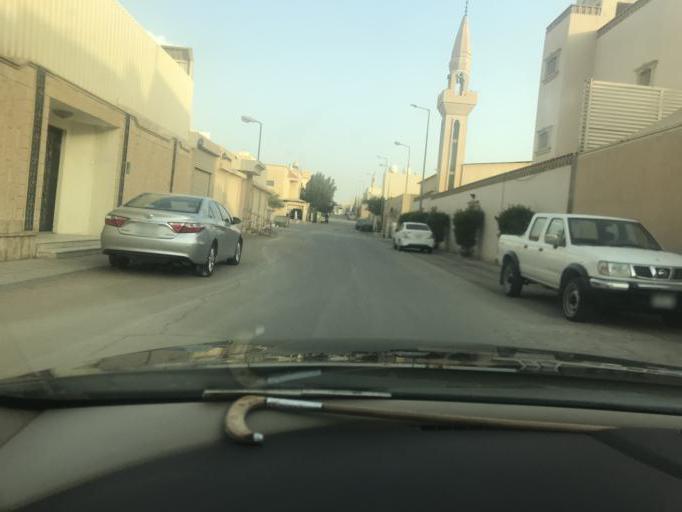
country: SA
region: Ar Riyad
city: Riyadh
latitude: 24.7371
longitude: 46.7760
